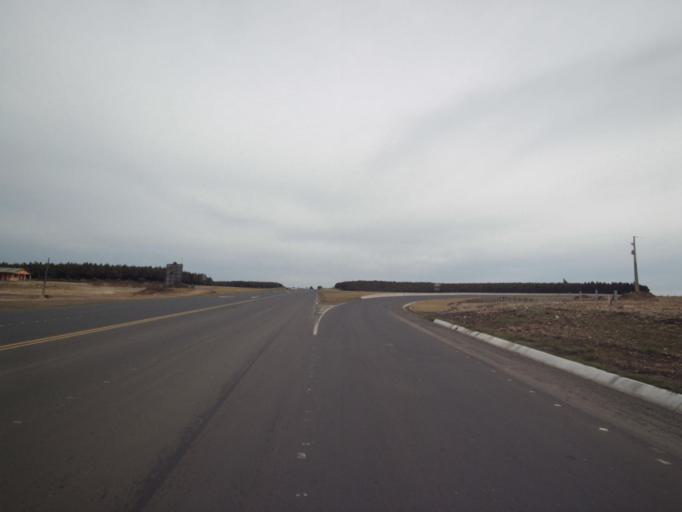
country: BR
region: Santa Catarina
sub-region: Cacador
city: Cacador
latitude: -26.6087
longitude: -51.4771
